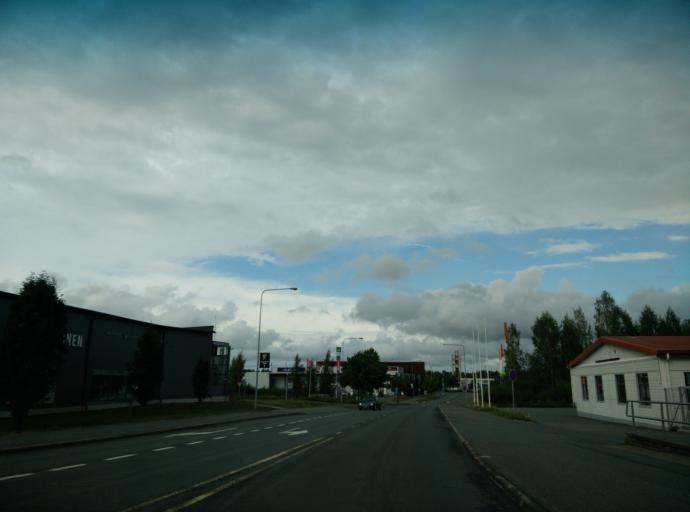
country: FI
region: Haeme
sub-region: Haemeenlinna
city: Haemeenlinna
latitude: 61.0051
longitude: 24.4185
